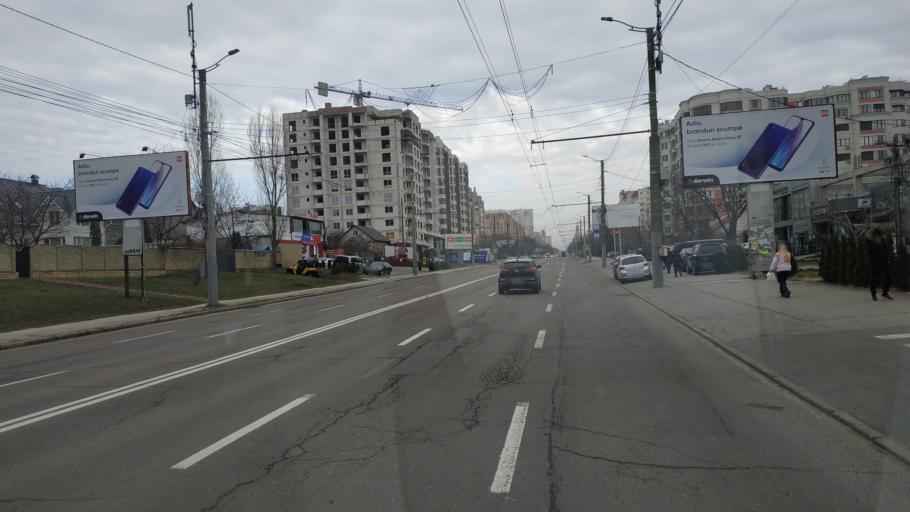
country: MD
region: Chisinau
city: Vatra
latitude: 47.0331
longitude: 28.7806
